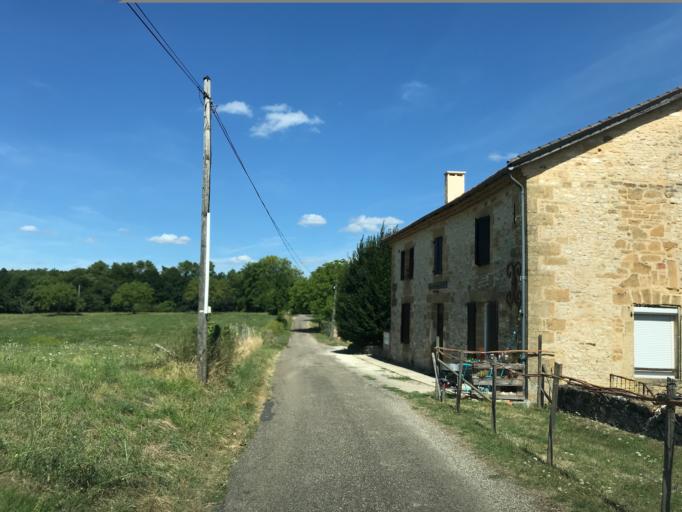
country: FR
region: Aquitaine
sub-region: Departement de la Dordogne
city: Sarlat-la-Caneda
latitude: 44.9091
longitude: 1.1837
